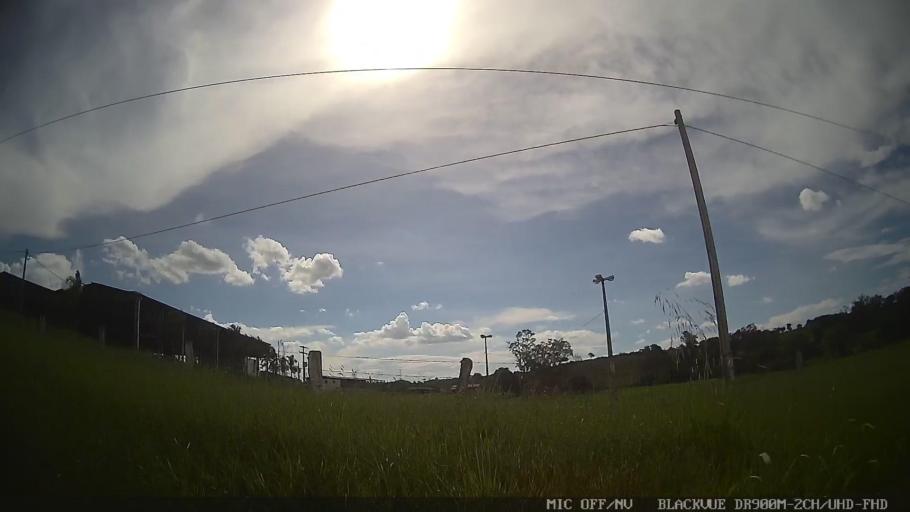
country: BR
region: Sao Paulo
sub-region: Conchas
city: Conchas
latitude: -23.0291
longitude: -47.9954
